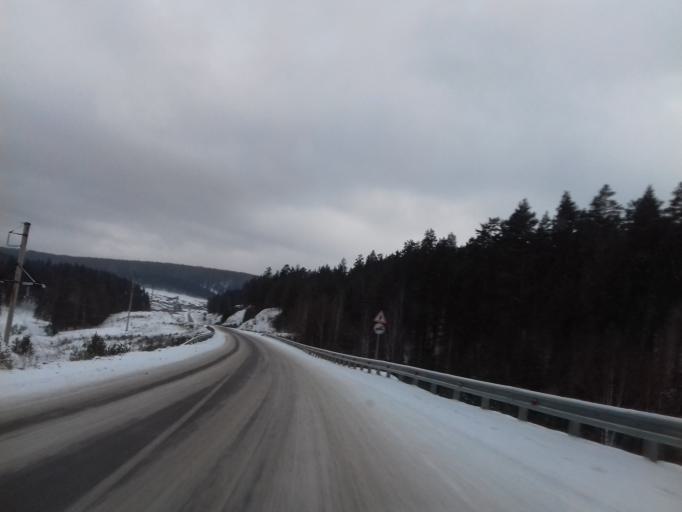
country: RU
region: Bashkortostan
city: Verkhniy Avzyan
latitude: 53.3388
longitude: 57.6353
